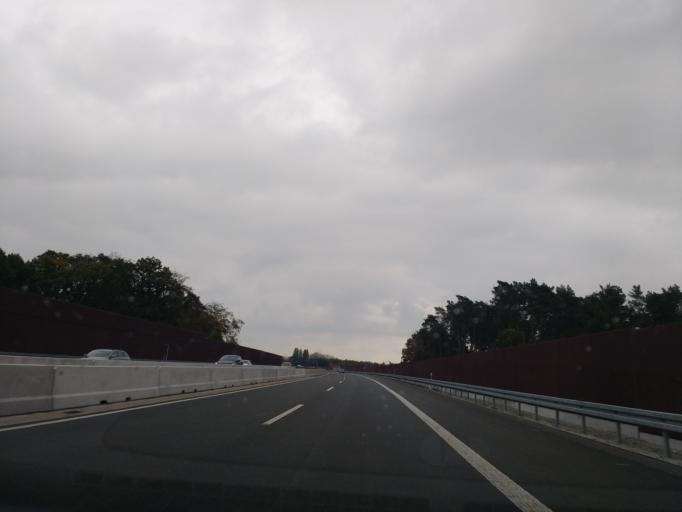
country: DE
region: North Rhine-Westphalia
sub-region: Regierungsbezirk Detmold
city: Steinhagen
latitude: 51.9785
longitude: 8.4658
